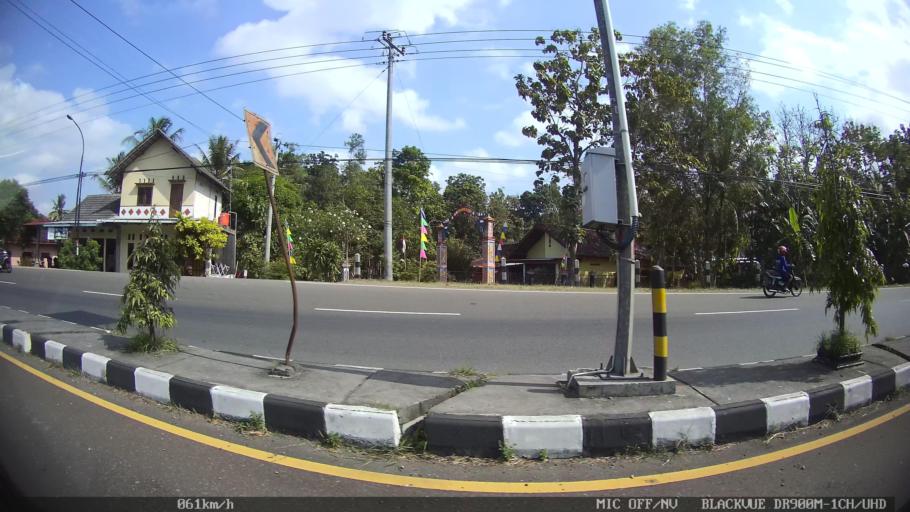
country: ID
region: Daerah Istimewa Yogyakarta
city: Srandakan
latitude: -7.8568
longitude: 110.2134
